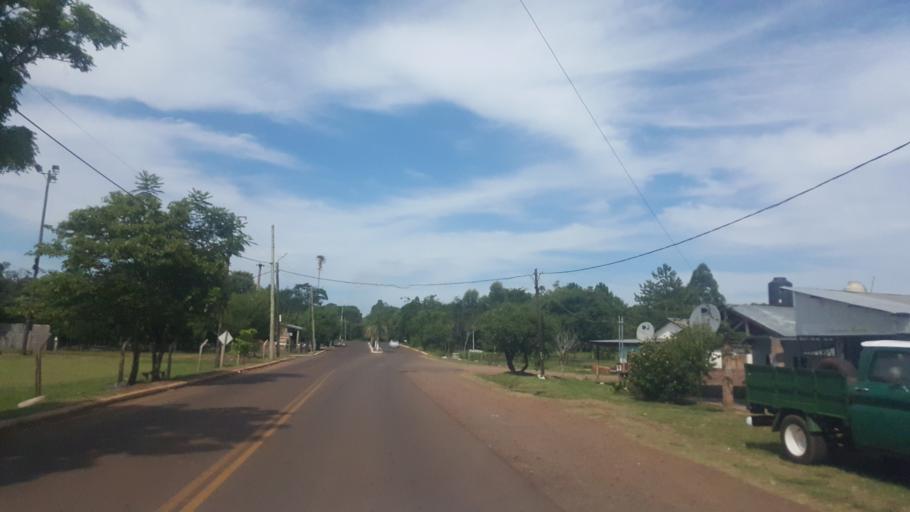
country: AR
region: Misiones
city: Cerro Cora
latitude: -27.5112
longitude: -55.6072
